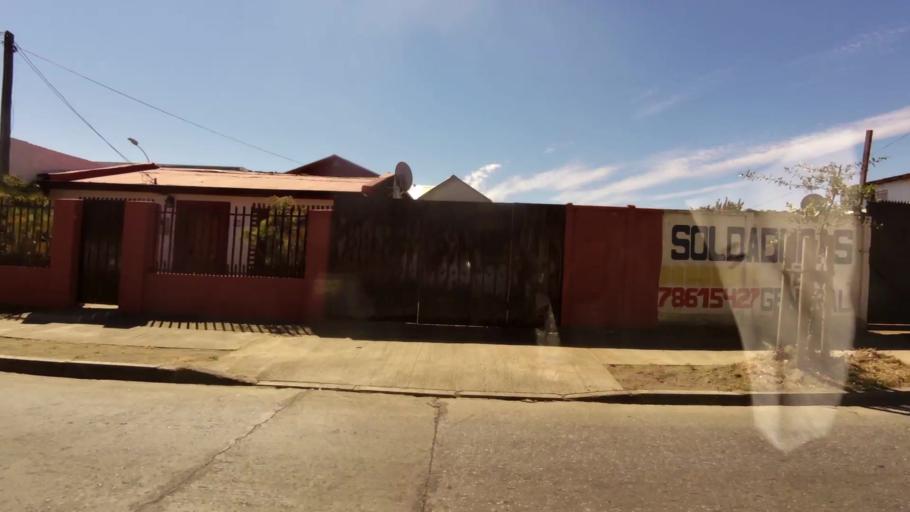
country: CL
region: Biobio
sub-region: Provincia de Concepcion
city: Penco
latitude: -36.7368
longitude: -72.9899
